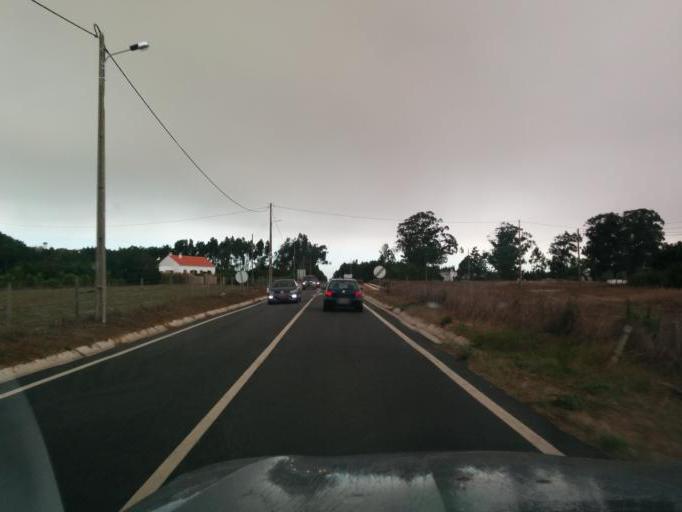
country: PT
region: Beja
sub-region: Odemira
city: Vila Nova de Milfontes
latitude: 37.6573
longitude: -8.7595
